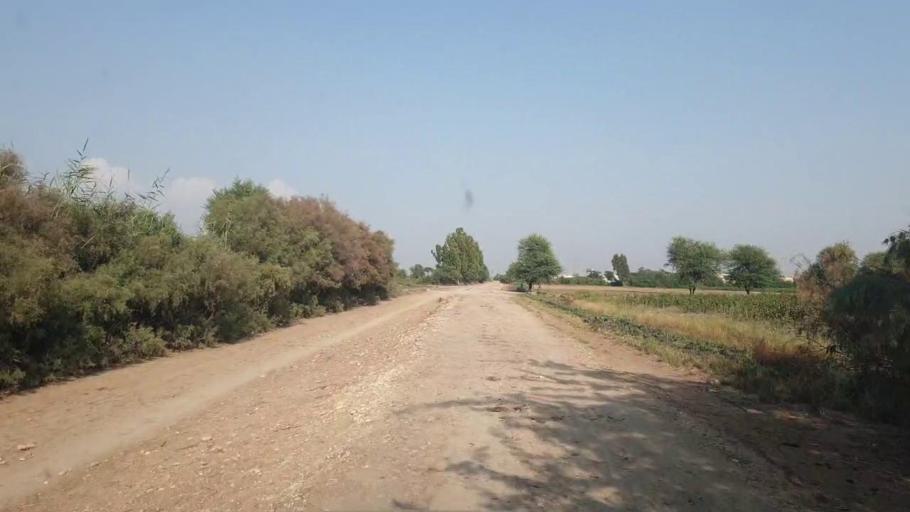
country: PK
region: Sindh
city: Sanghar
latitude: 26.0568
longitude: 68.8795
